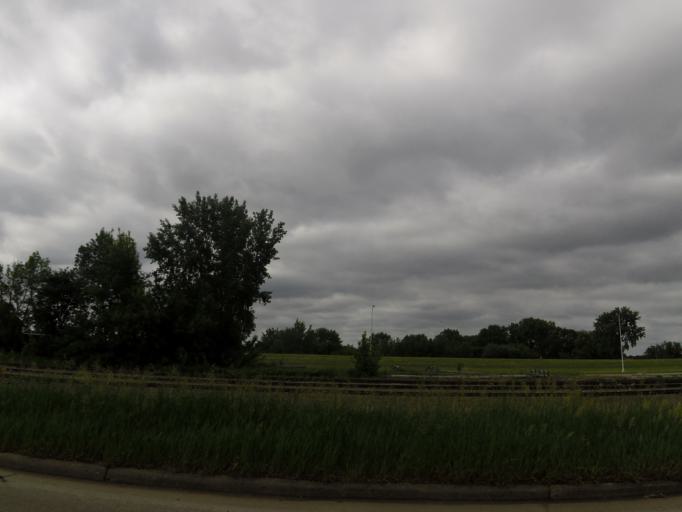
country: US
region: Minnesota
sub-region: Polk County
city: East Grand Forks
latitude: 47.9261
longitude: -97.0131
